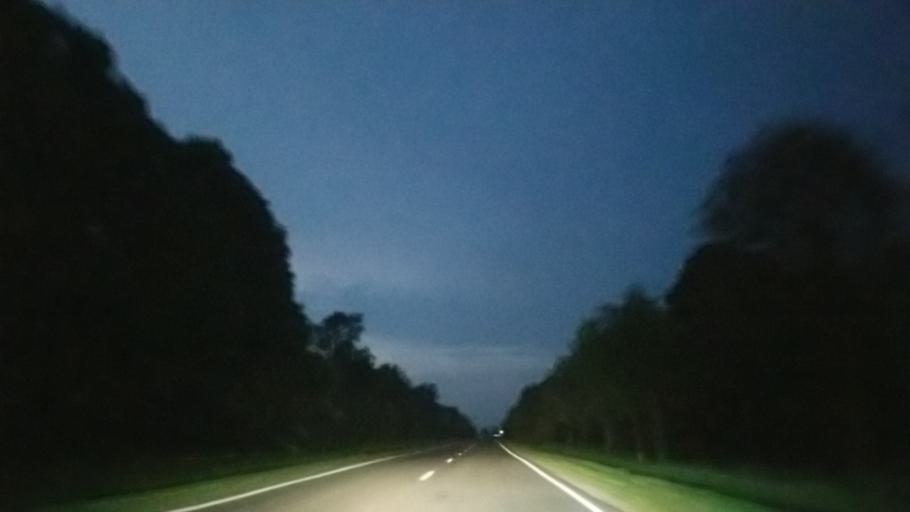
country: PL
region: Lublin Voivodeship
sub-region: Powiat bialski
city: Koden
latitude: 51.9138
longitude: 23.6579
